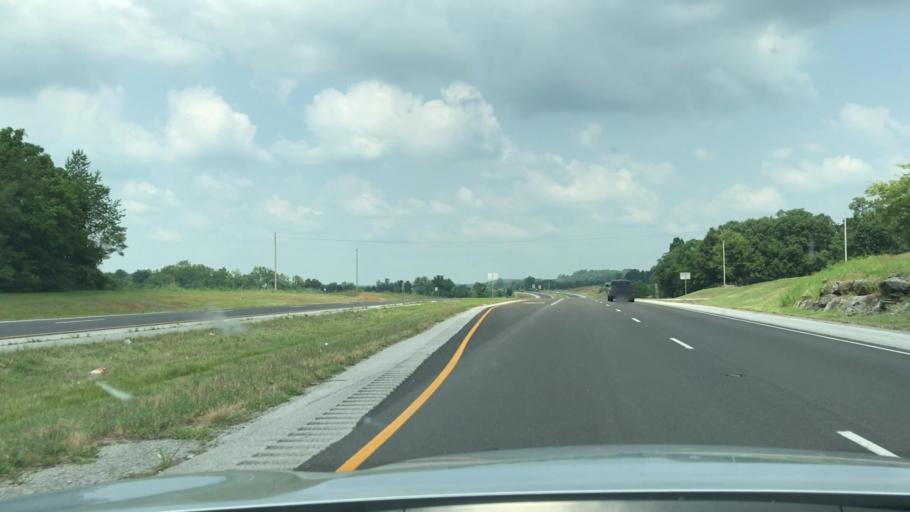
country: US
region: Kentucky
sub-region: Todd County
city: Elkton
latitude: 36.8047
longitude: -87.1091
